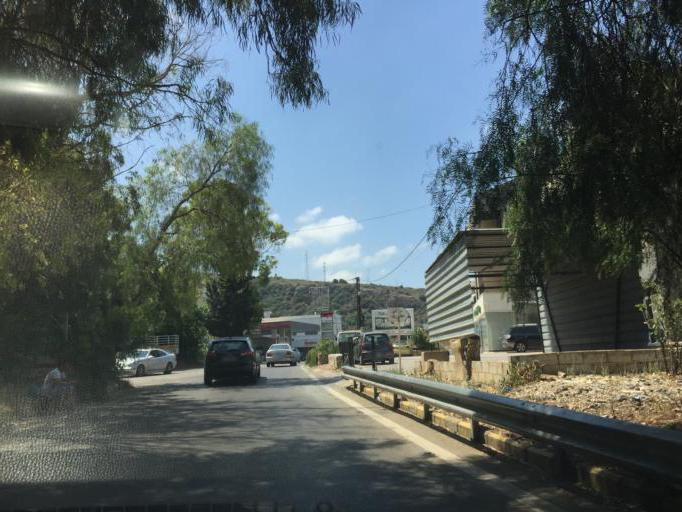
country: LB
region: Mont-Liban
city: Beit ed Dine
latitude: 33.7077
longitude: 35.4500
